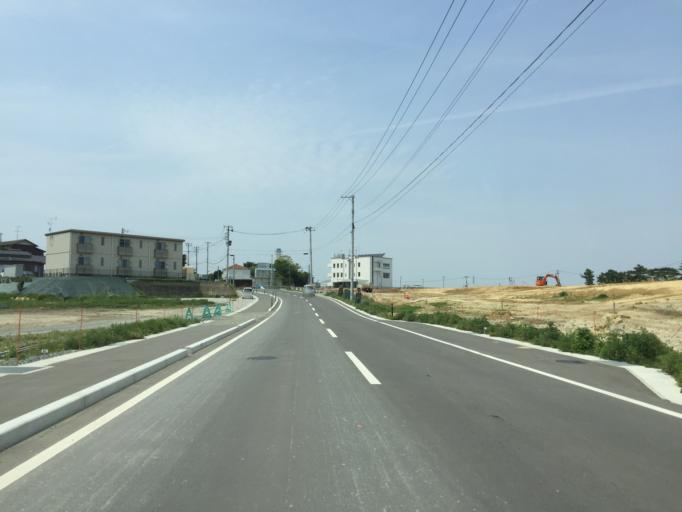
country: JP
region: Miyagi
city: Marumori
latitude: 37.8278
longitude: 140.9645
